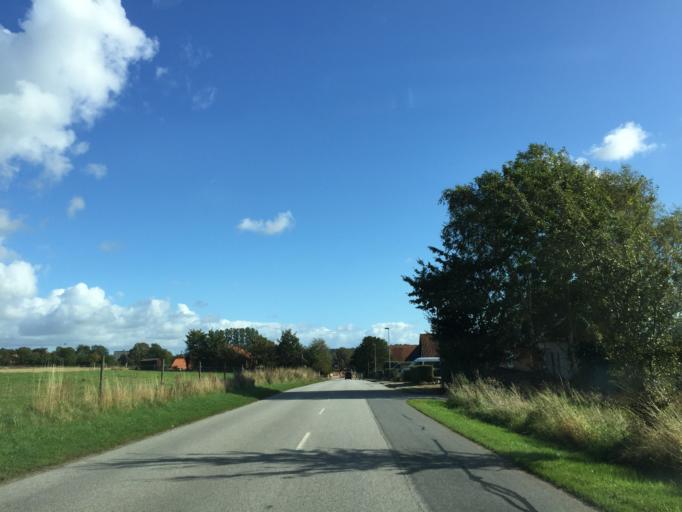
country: DK
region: Central Jutland
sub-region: Viborg Kommune
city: Bjerringbro
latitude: 56.4395
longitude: 9.5456
